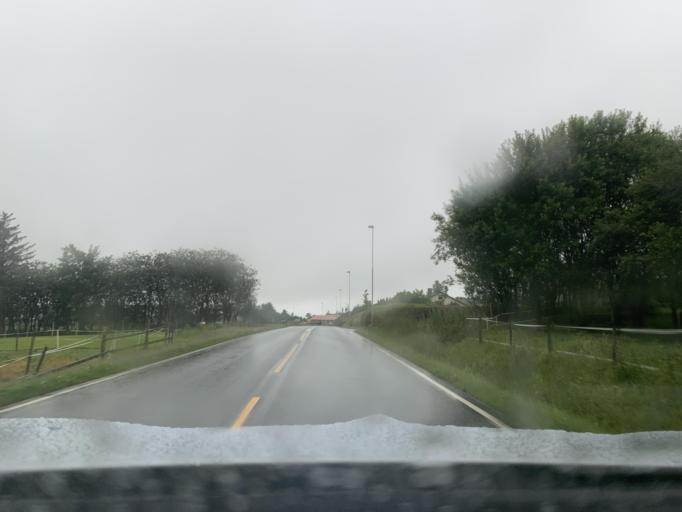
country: NO
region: Rogaland
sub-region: Time
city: Bryne
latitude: 58.7395
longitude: 5.6185
